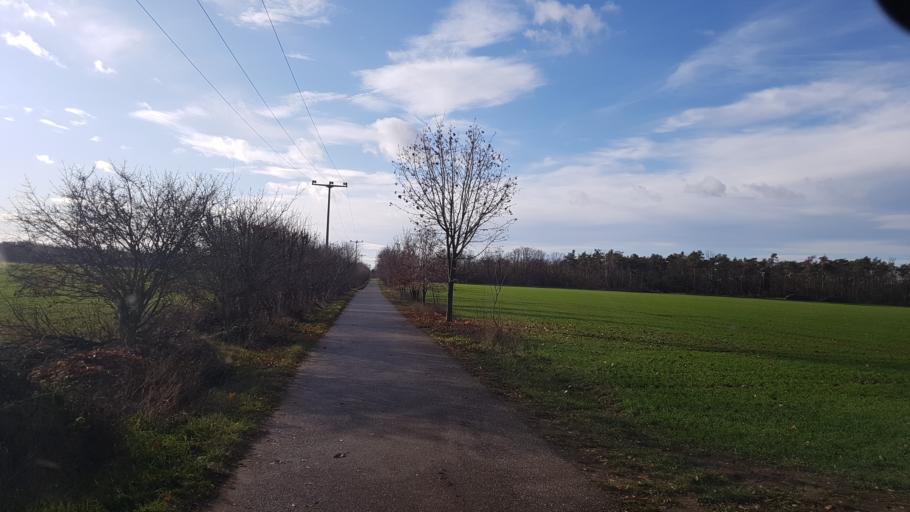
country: DE
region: Brandenburg
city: Falkenberg
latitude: 51.5996
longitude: 13.2796
